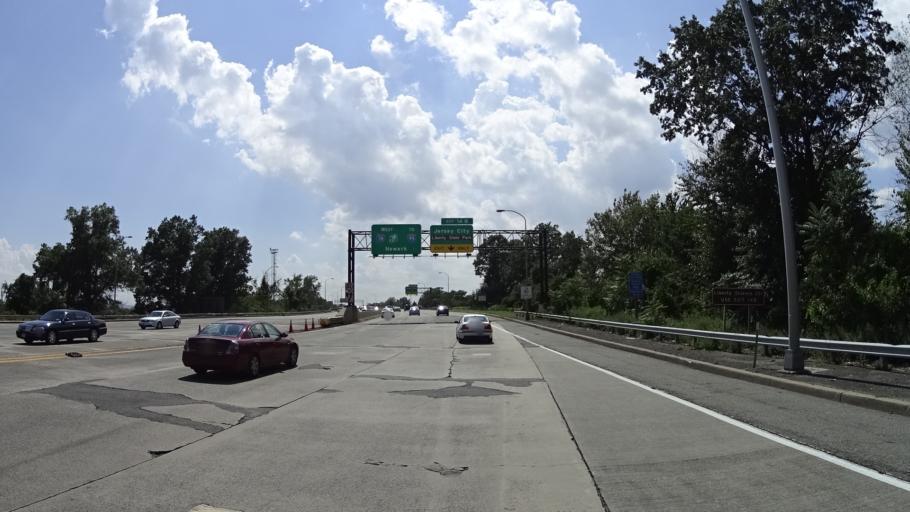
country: US
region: New Jersey
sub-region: Hudson County
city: Jersey City
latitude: 40.7058
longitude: -74.0633
